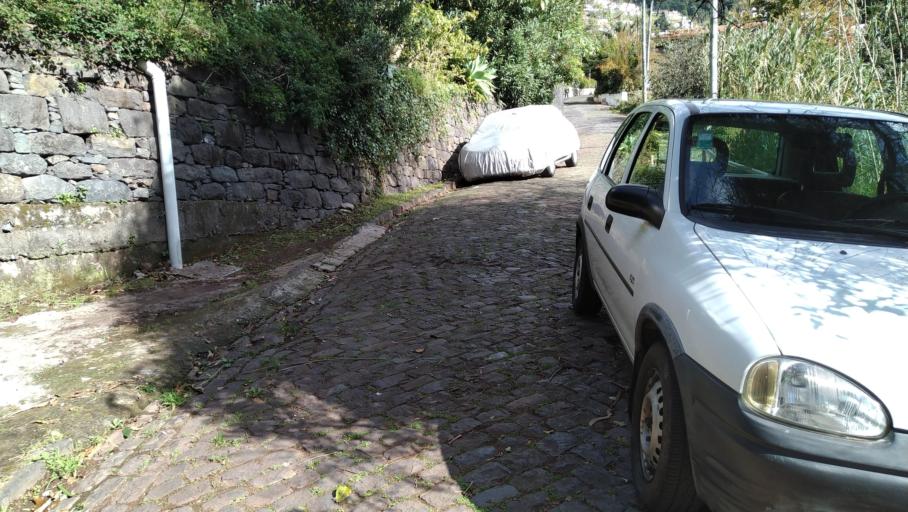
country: PT
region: Madeira
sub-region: Funchal
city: Nossa Senhora do Monte
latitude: 32.6584
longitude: -16.8784
